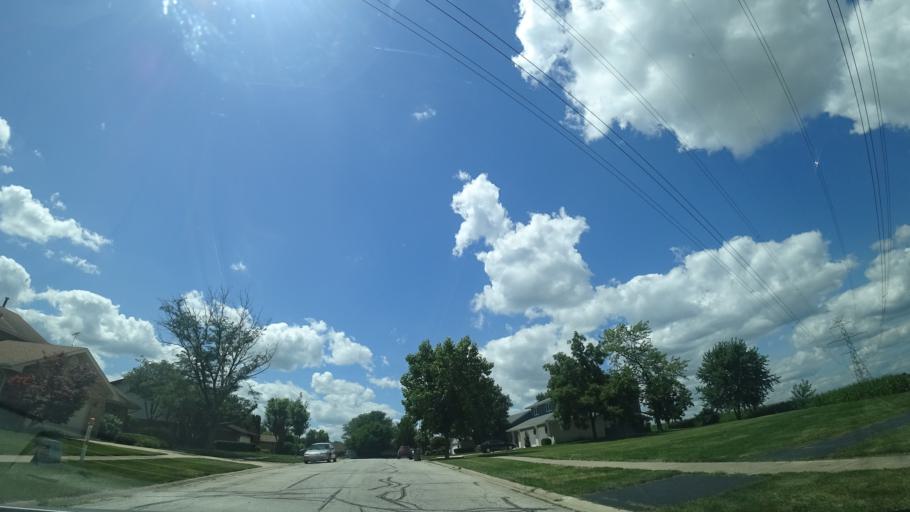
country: US
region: Illinois
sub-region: Will County
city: Homer Glen
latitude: 41.5783
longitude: -87.9003
